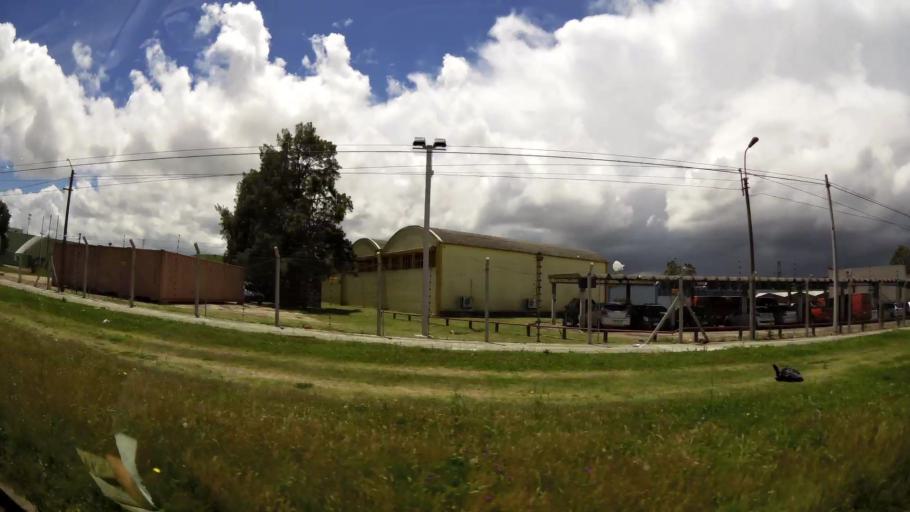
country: UY
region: Montevideo
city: Montevideo
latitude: -34.8352
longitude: -56.1870
